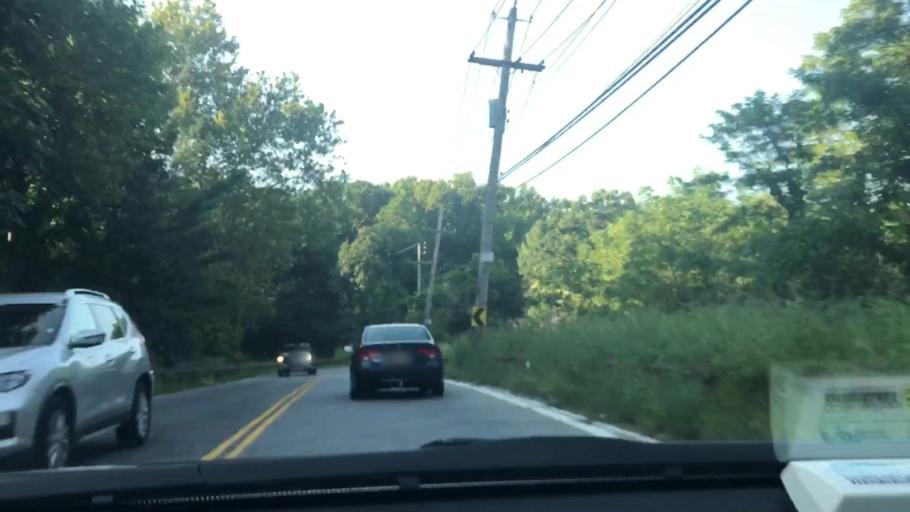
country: US
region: New York
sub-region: Westchester County
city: Pelham Manor
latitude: 40.8798
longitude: -73.7957
